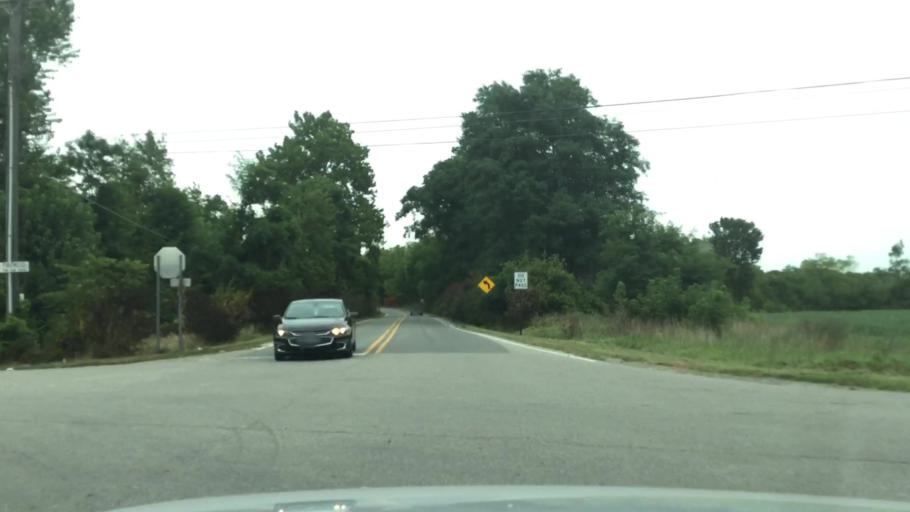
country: US
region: Michigan
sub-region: Washtenaw County
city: Milan
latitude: 42.1340
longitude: -83.6779
